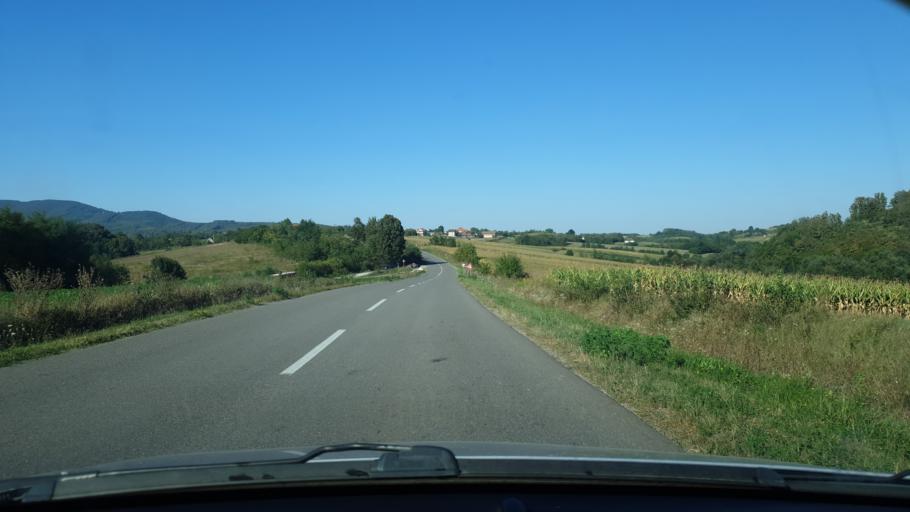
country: RS
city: Bukor
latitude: 44.5437
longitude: 19.5163
